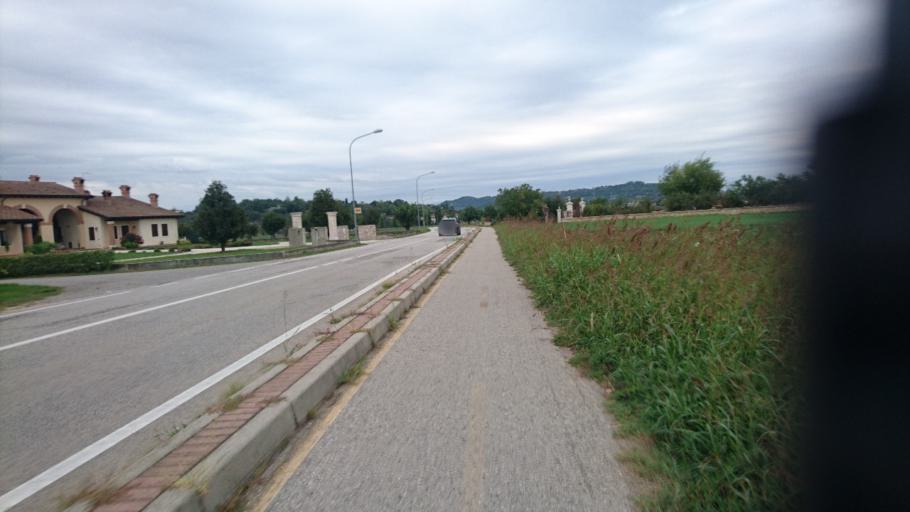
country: IT
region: Veneto
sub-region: Provincia di Vicenza
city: Tavernelle
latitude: 45.5151
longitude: 11.4299
